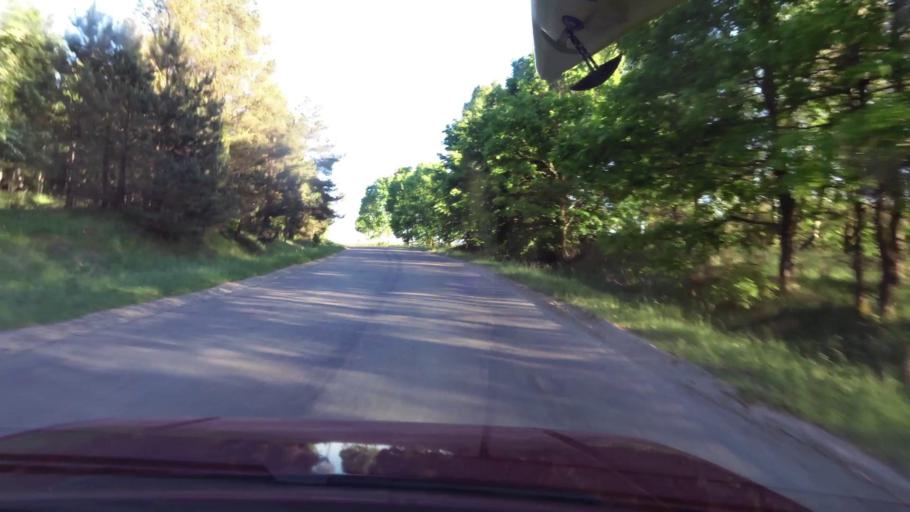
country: PL
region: West Pomeranian Voivodeship
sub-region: Powiat szczecinecki
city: Bialy Bor
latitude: 53.9146
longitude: 16.8061
